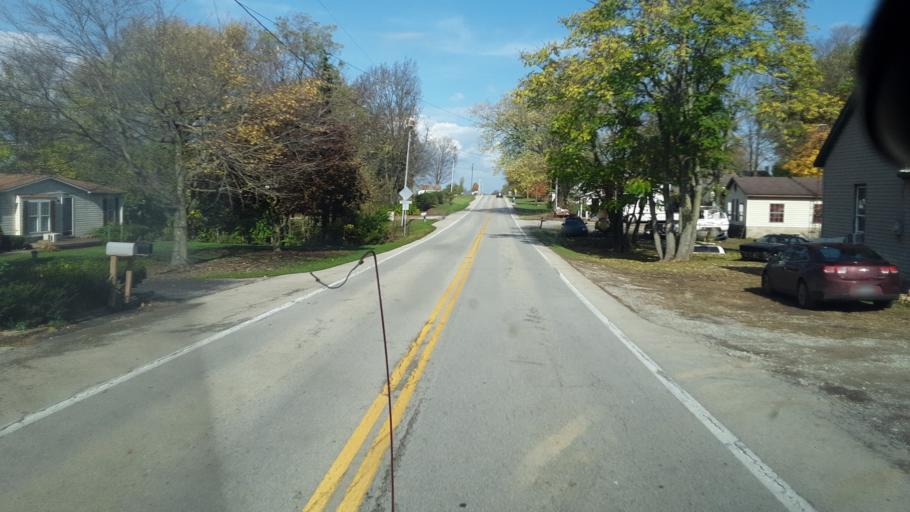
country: US
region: Ohio
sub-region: Clinton County
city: Sabina
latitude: 39.5378
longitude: -83.7065
